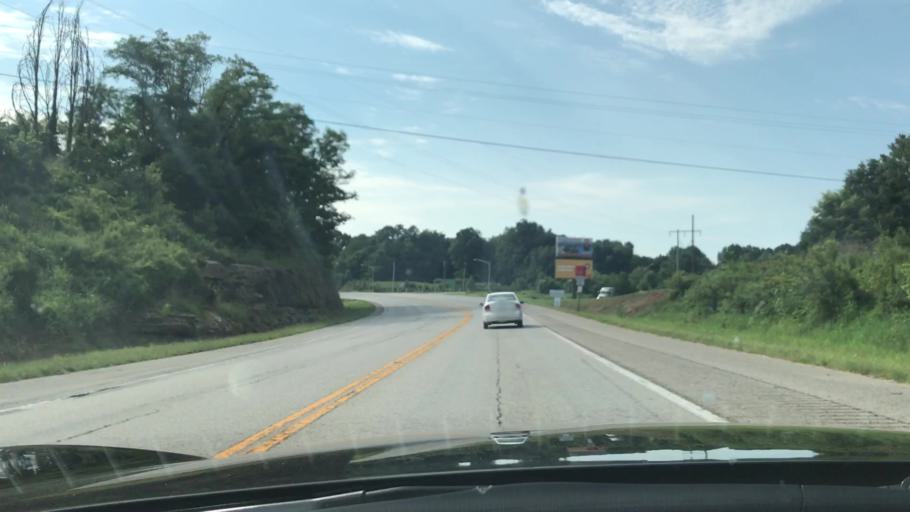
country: US
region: Kentucky
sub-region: Green County
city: Greensburg
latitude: 37.2757
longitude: -85.5103
